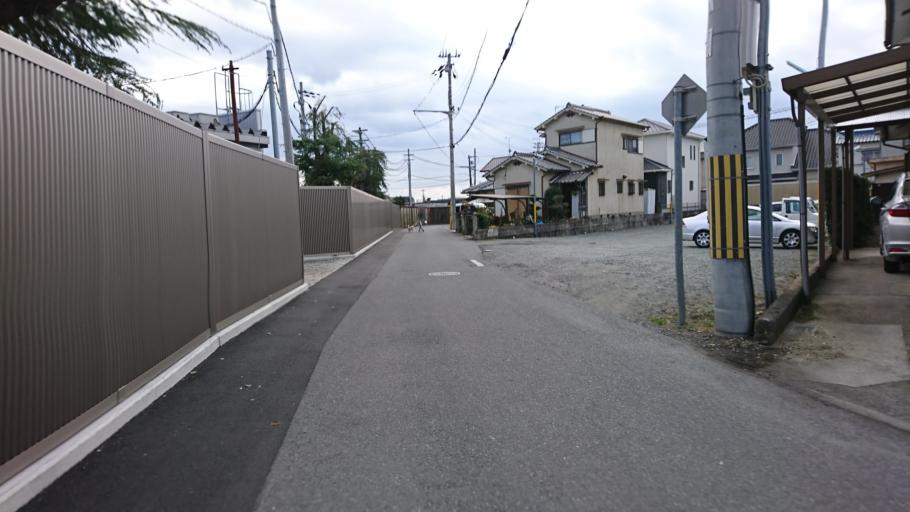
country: JP
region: Hyogo
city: Kakogawacho-honmachi
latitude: 34.7796
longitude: 134.8245
